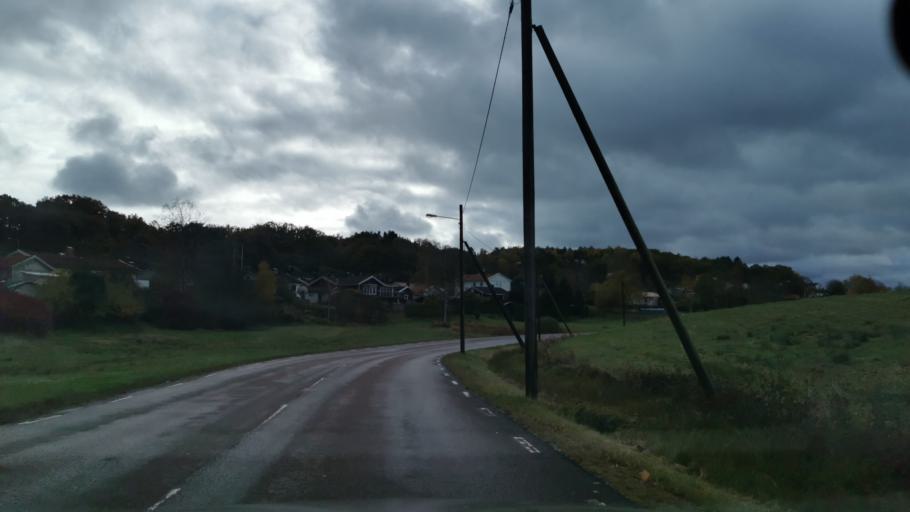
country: SE
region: Vaestra Goetaland
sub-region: Partille Kommun
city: Partille
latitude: 57.7245
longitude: 12.0914
